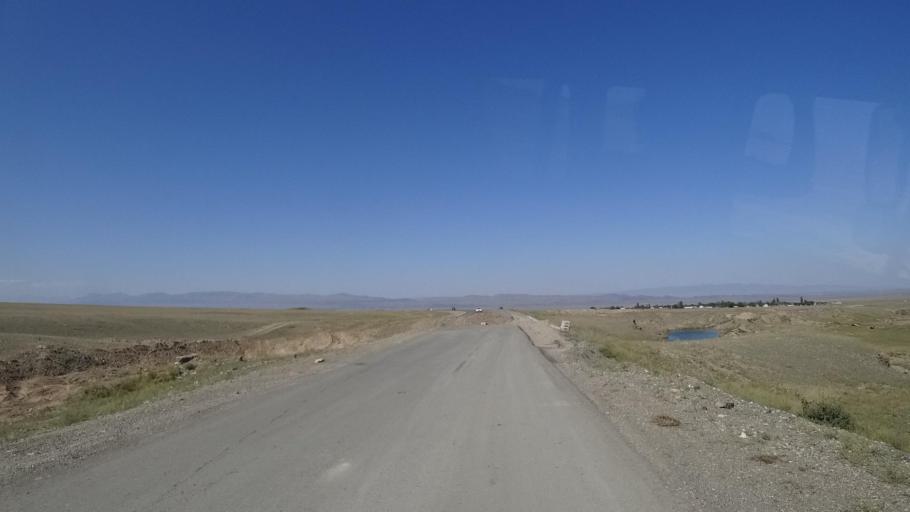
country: KZ
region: Almaty Oblysy
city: Kegen
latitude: 43.1999
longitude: 79.1227
